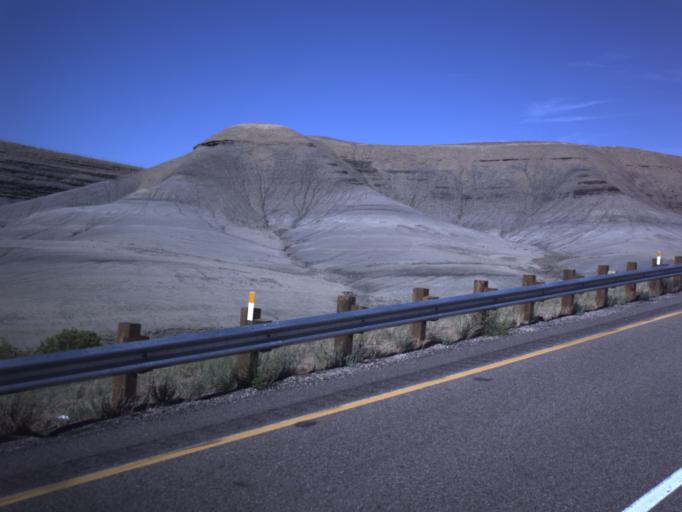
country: US
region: Utah
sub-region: Carbon County
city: East Carbon City
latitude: 38.9375
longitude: -110.3402
